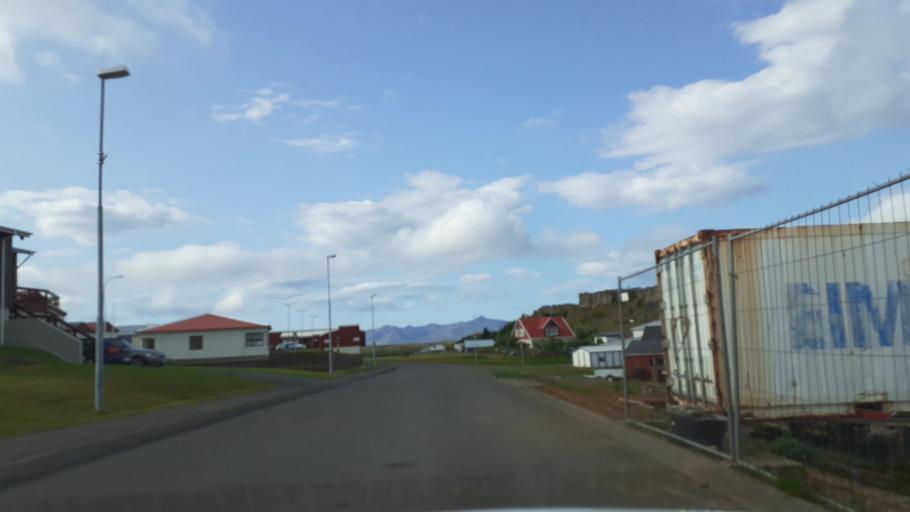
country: IS
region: East
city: Reydarfjoerdur
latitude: 64.6562
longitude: -14.2788
